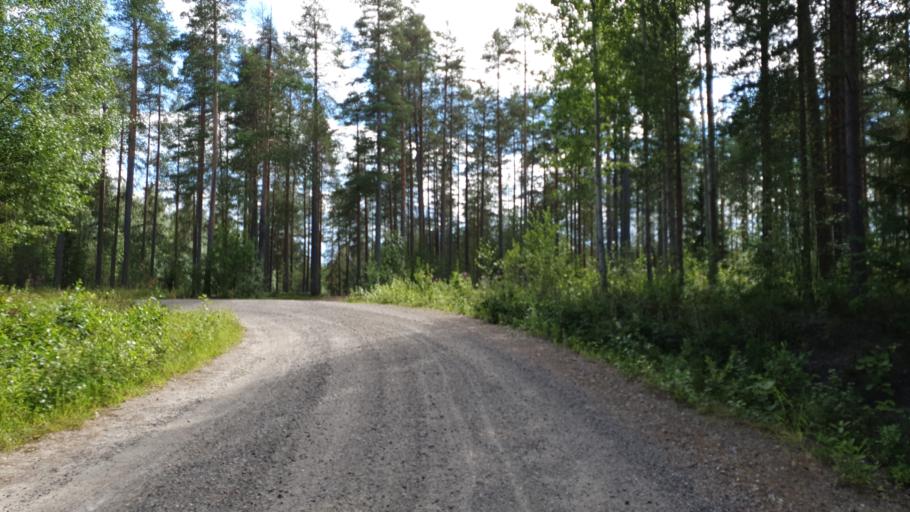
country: FI
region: Kainuu
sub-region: Kehys-Kainuu
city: Kuhmo
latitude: 64.1152
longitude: 29.5166
